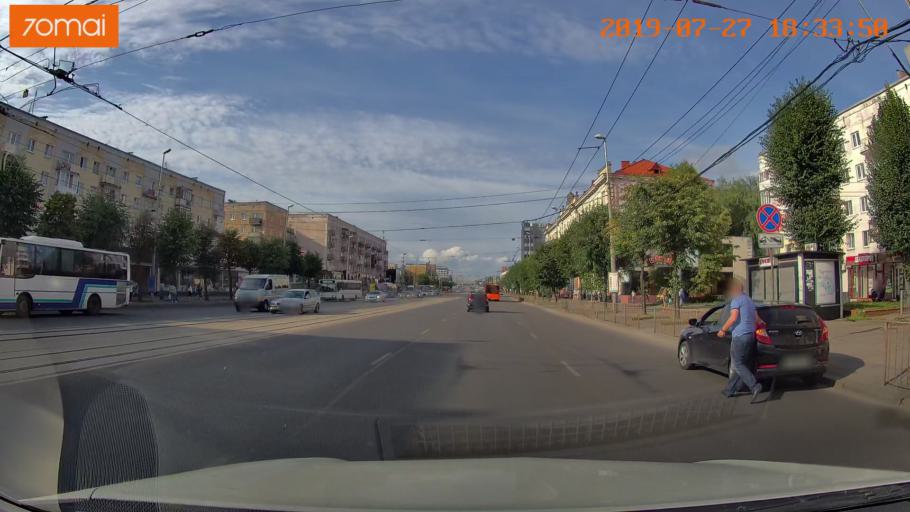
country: RU
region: Kaliningrad
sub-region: Gorod Kaliningrad
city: Kaliningrad
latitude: 54.7001
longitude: 20.5037
